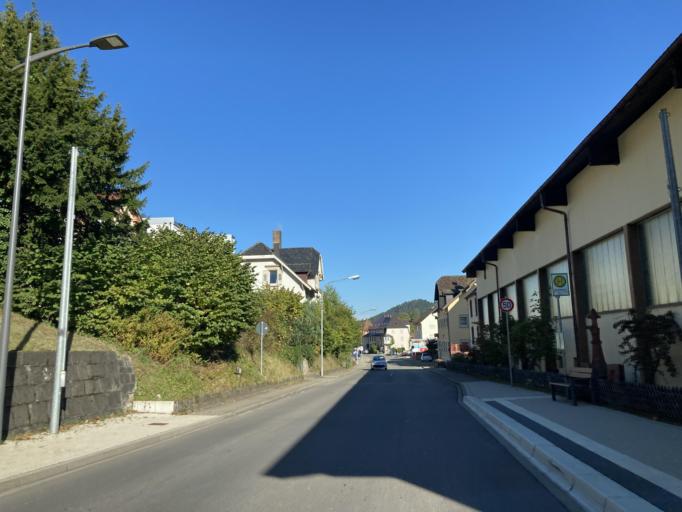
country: DE
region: Baden-Wuerttemberg
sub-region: Freiburg Region
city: Hornberg
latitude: 48.2157
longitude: 8.2264
